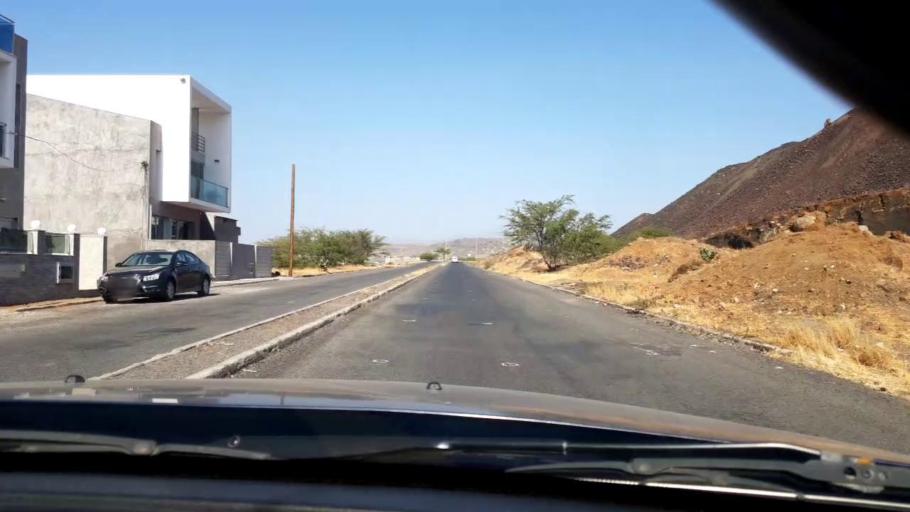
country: CV
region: Praia
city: Praia
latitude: 14.9136
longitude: -23.5397
